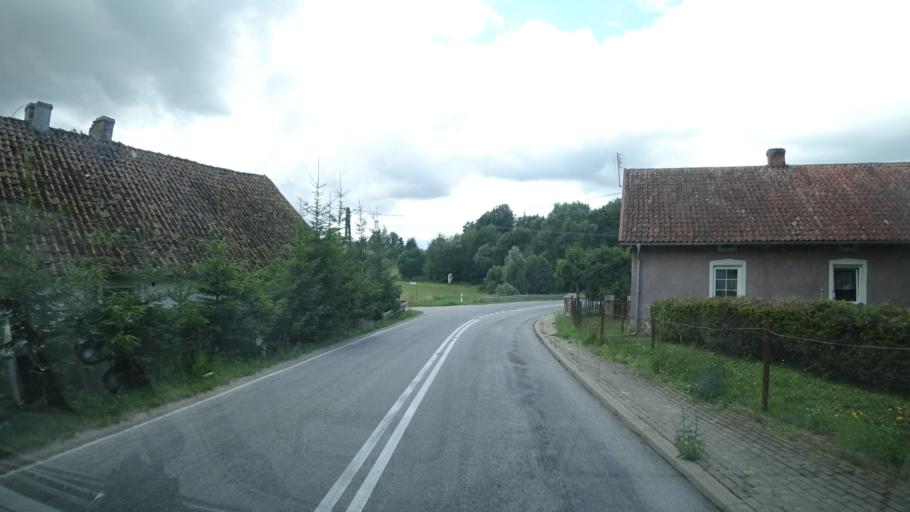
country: PL
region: Warmian-Masurian Voivodeship
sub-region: Powiat goldapski
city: Goldap
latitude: 54.2107
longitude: 22.2108
